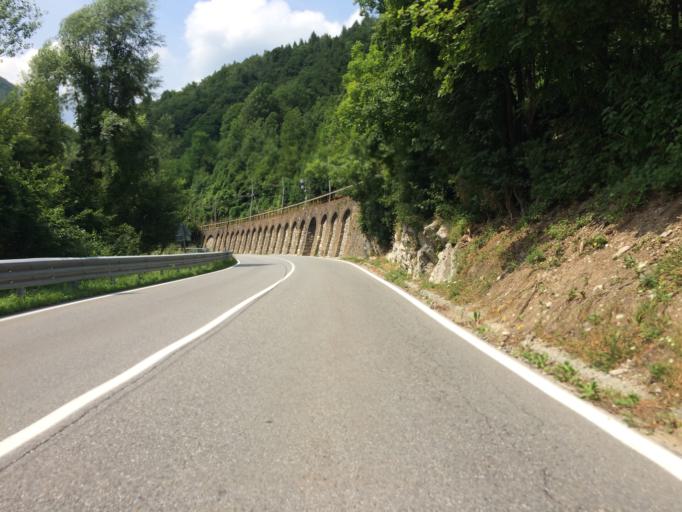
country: IT
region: Piedmont
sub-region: Provincia di Cuneo
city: Vernante
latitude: 44.2589
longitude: 7.5240
